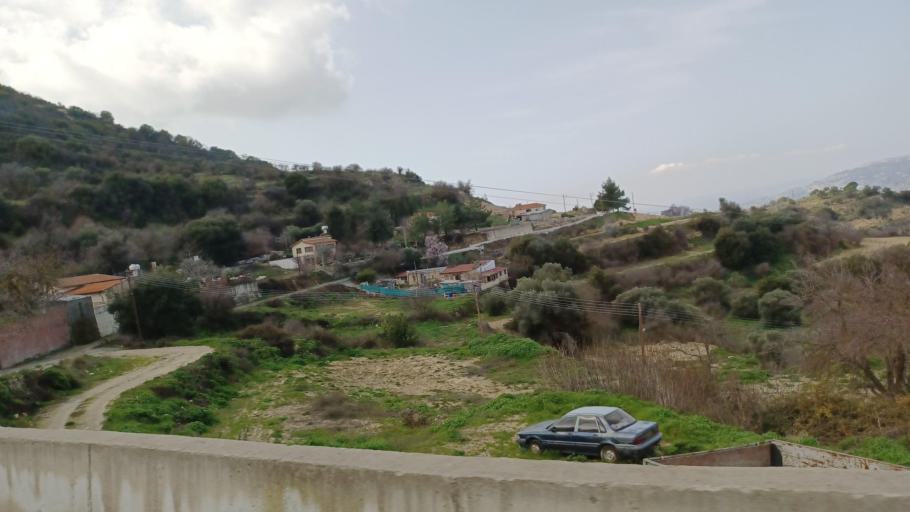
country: CY
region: Limassol
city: Pachna
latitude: 34.7799
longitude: 32.7370
